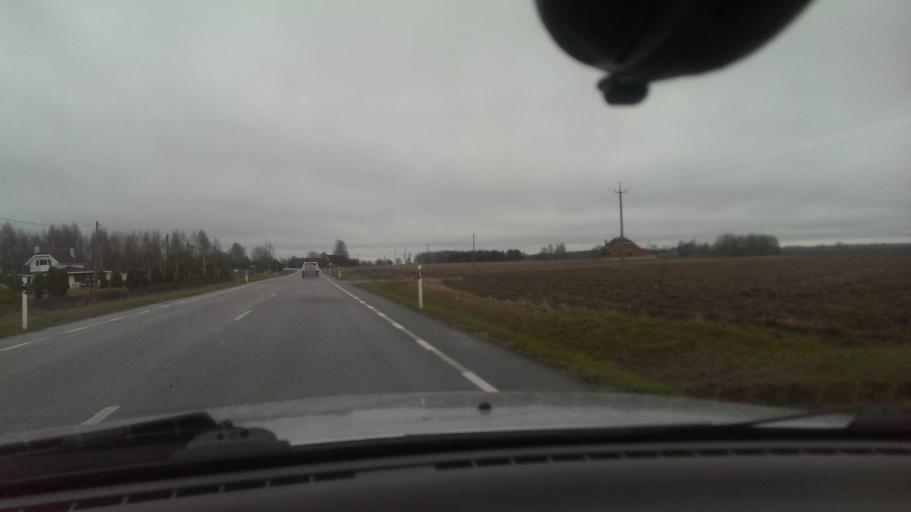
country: EE
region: Tartu
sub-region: Tartu linn
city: Tartu
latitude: 58.3887
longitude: 26.8040
